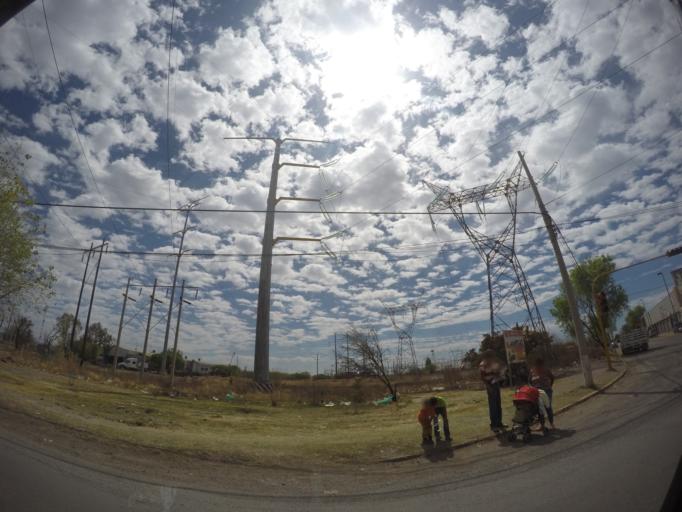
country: MX
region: Guanajuato
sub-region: Leon
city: Santa Ana
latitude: 21.0592
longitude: -101.6867
